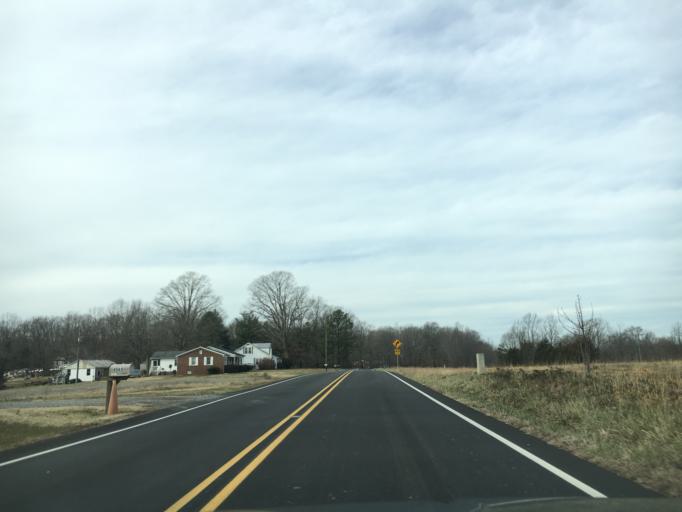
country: US
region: Virginia
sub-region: Goochland County
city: Goochland
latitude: 37.8166
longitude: -77.8748
